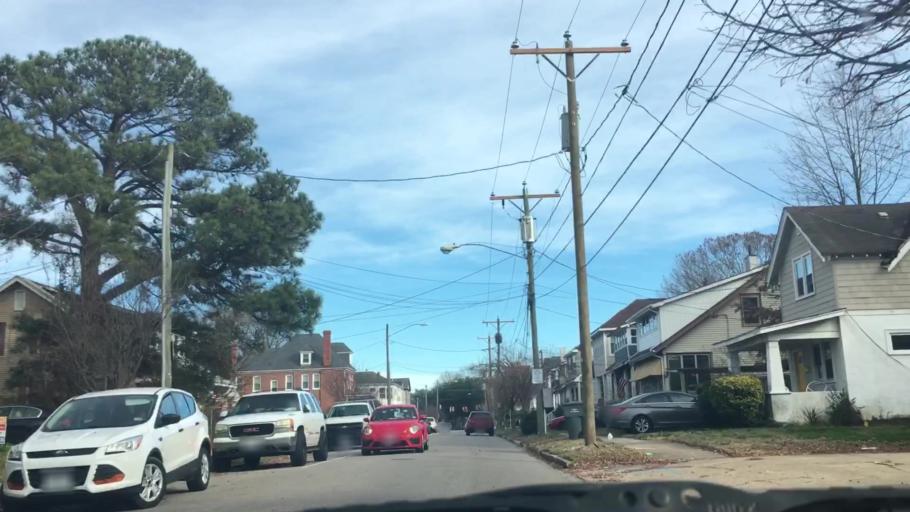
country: US
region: Virginia
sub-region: City of Norfolk
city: Norfolk
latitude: 36.8805
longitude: -76.2845
